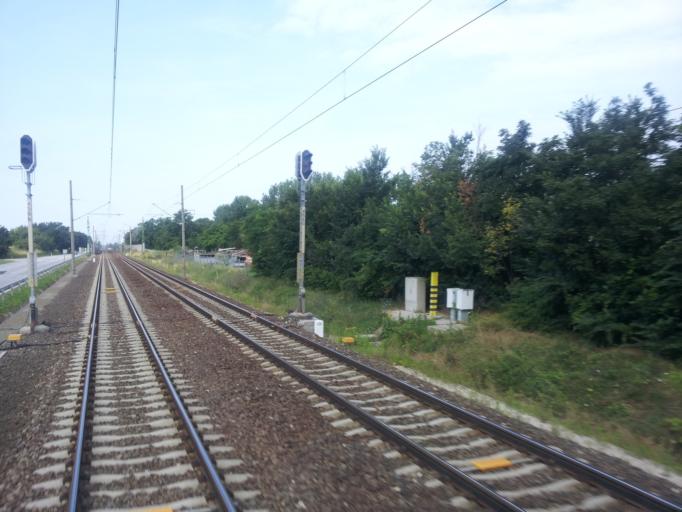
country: HU
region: Fejer
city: Kapolnasnyek
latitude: 47.2315
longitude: 18.6727
